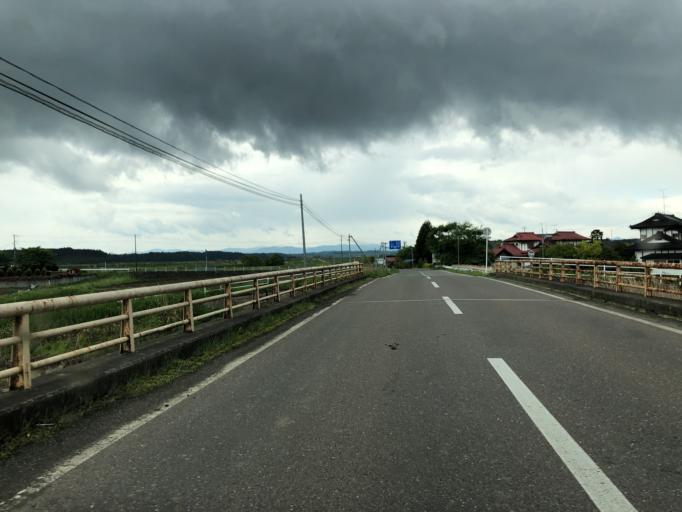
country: JP
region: Fukushima
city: Ishikawa
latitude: 37.1583
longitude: 140.3857
